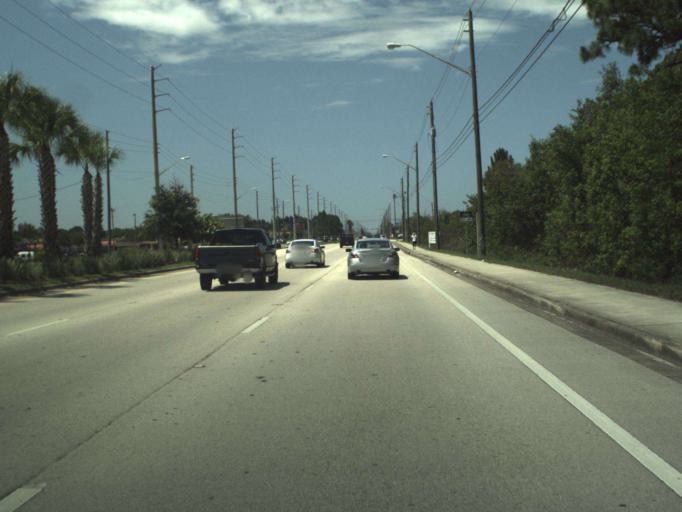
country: US
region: Florida
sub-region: Saint Lucie County
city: Indian River Estates
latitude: 27.3387
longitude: -80.3258
